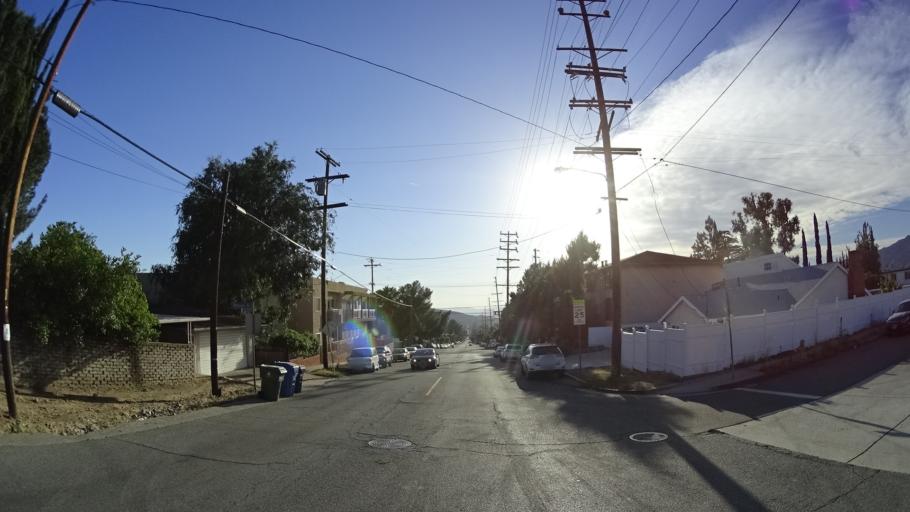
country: US
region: California
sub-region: Los Angeles County
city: La Crescenta-Montrose
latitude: 34.2560
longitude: -118.2902
